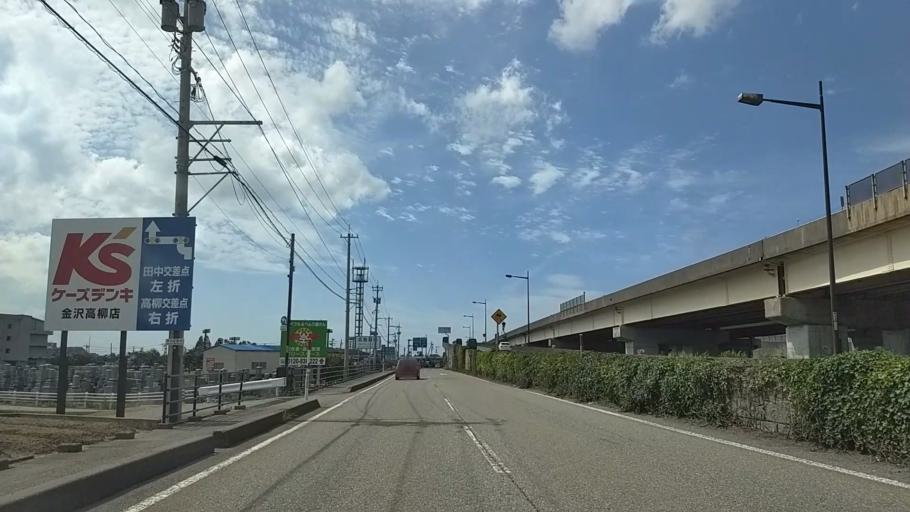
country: JP
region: Ishikawa
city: Kanazawa-shi
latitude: 36.6027
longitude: 136.6624
